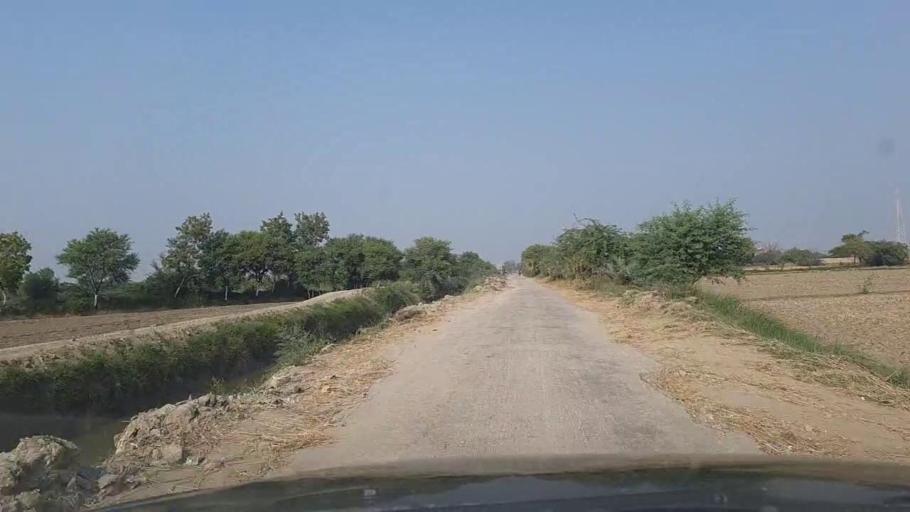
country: PK
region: Sindh
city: Mirpur Batoro
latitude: 24.7204
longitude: 68.2558
